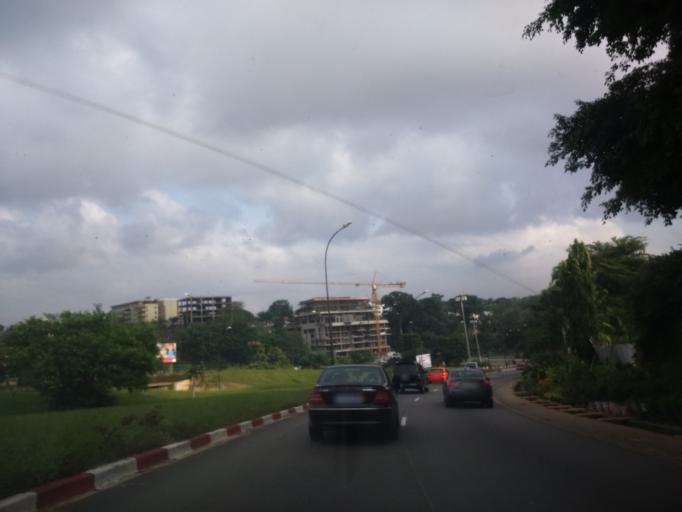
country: CI
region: Lagunes
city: Abidjan
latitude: 5.3361
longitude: -4.0091
